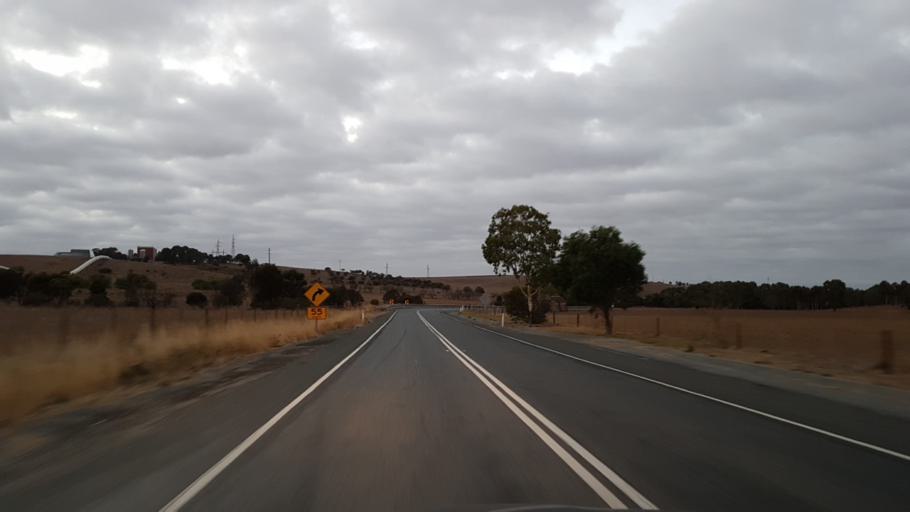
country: AU
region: South Australia
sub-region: Mount Barker
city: Callington
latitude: -35.0541
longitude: 139.0089
